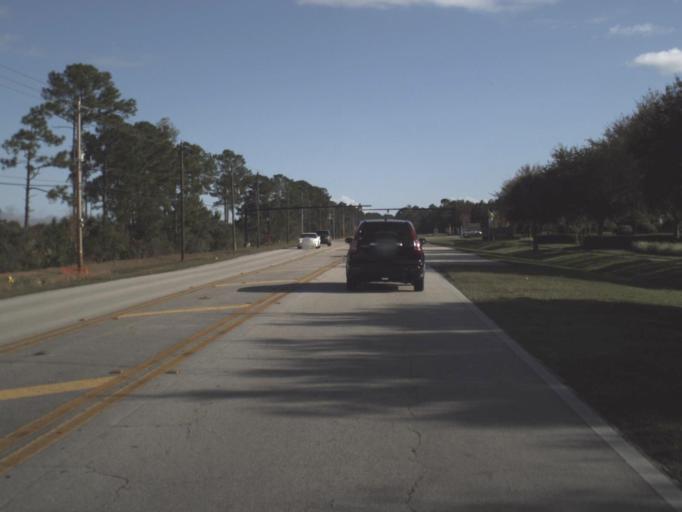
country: US
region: Florida
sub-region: Volusia County
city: Ormond Beach
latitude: 29.2482
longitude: -81.1073
